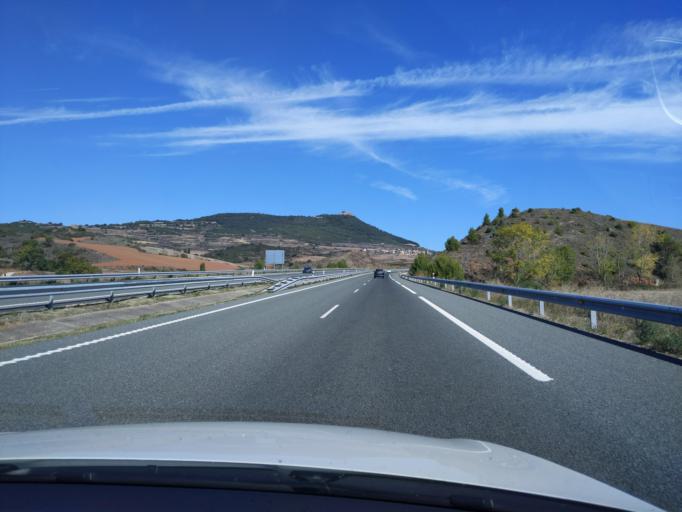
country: ES
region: Navarre
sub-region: Provincia de Navarra
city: Villamayor de Monjardin
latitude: 42.6110
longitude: -2.1124
